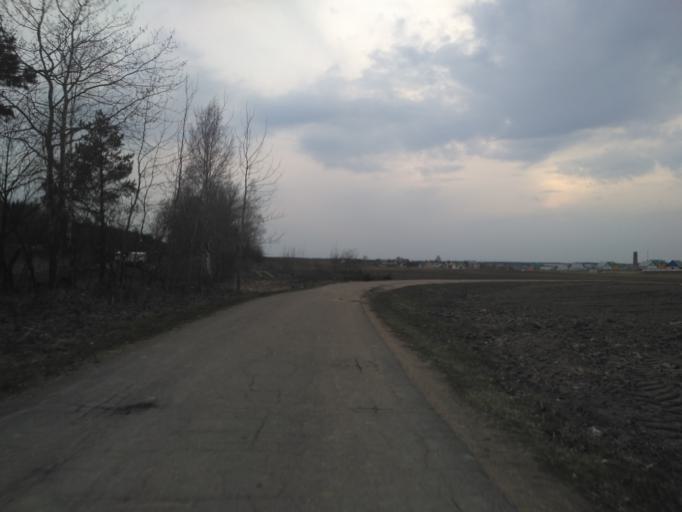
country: BY
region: Minsk
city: Slabada
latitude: 53.9952
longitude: 27.9021
